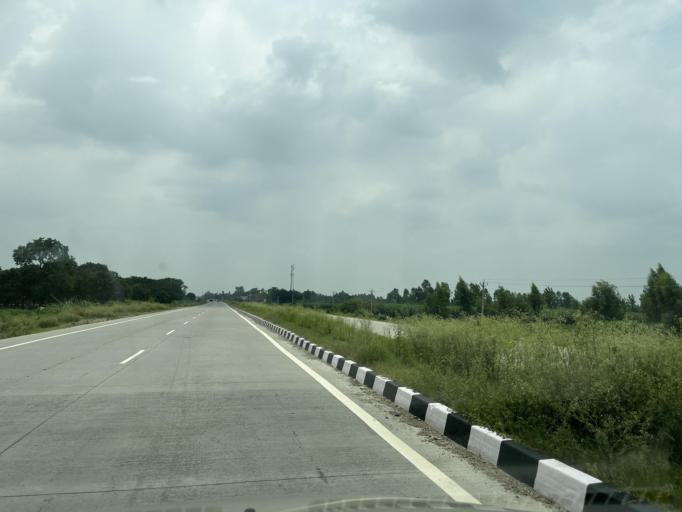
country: IN
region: Uttar Pradesh
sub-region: Bijnor
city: Najibabad
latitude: 29.5538
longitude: 78.3392
